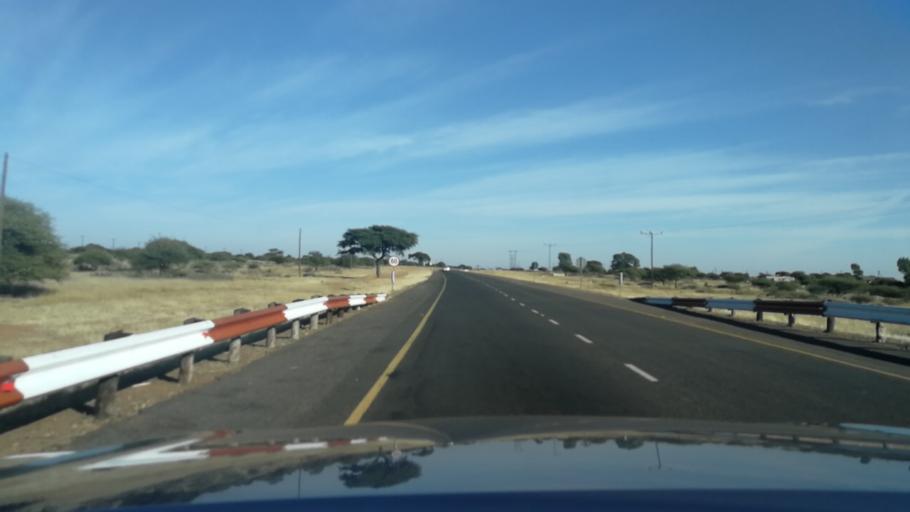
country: BW
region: South East
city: Janeng
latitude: -25.4685
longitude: 25.5531
